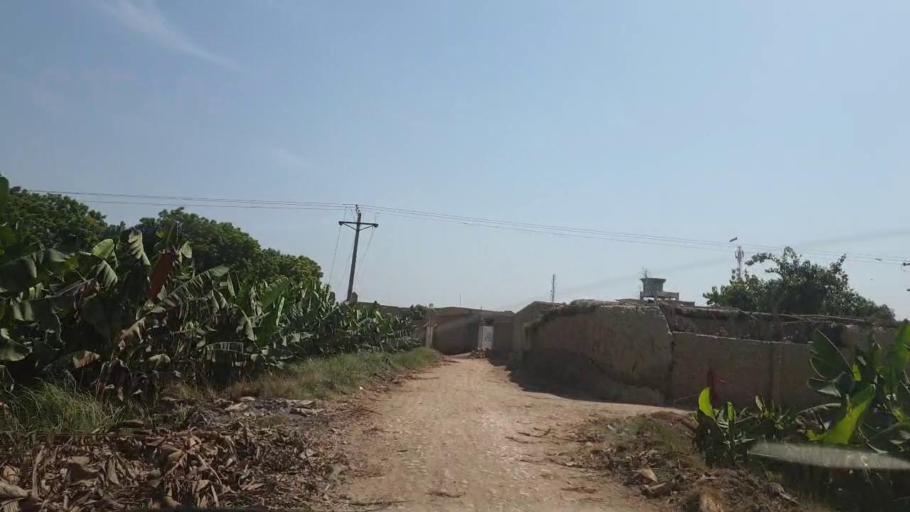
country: PK
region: Sindh
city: Tando Allahyar
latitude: 25.3899
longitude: 68.6737
